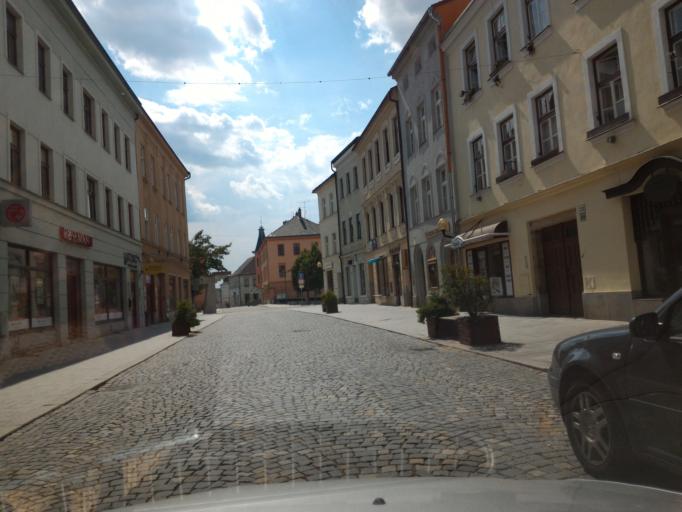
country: CZ
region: Vysocina
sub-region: Okres Jihlava
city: Jihlava
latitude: 49.3959
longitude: 15.5872
